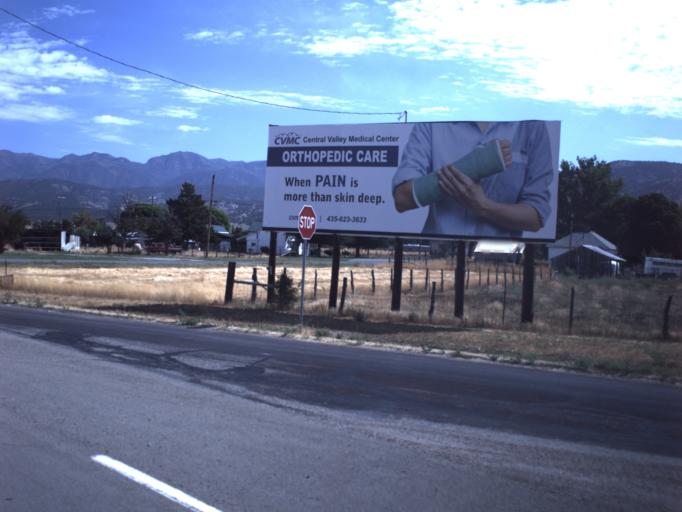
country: US
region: Utah
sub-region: Juab County
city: Nephi
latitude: 39.5598
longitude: -111.8621
